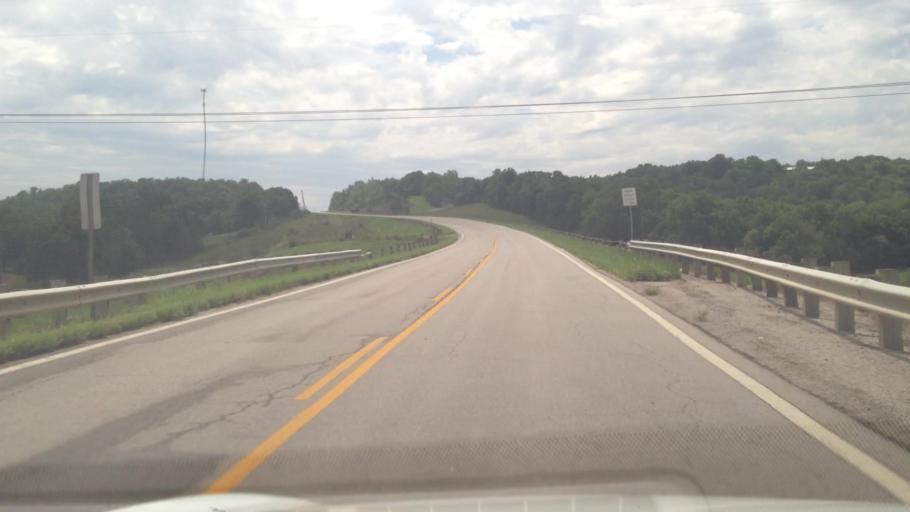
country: US
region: Kansas
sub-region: Bourbon County
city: Fort Scott
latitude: 37.8348
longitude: -94.9813
